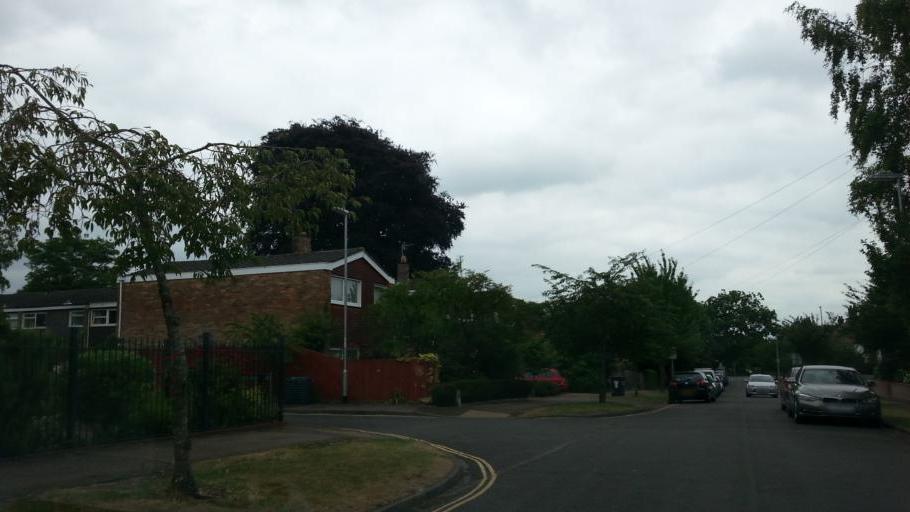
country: GB
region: England
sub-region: Cambridgeshire
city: Cambridge
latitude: 52.2187
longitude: 0.1280
